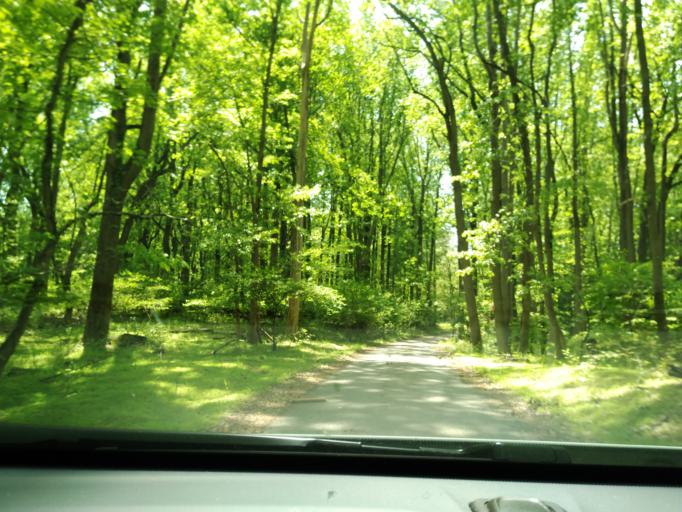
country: US
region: Maryland
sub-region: Prince George's County
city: Marlboro Meadows
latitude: 38.8575
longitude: -76.7113
